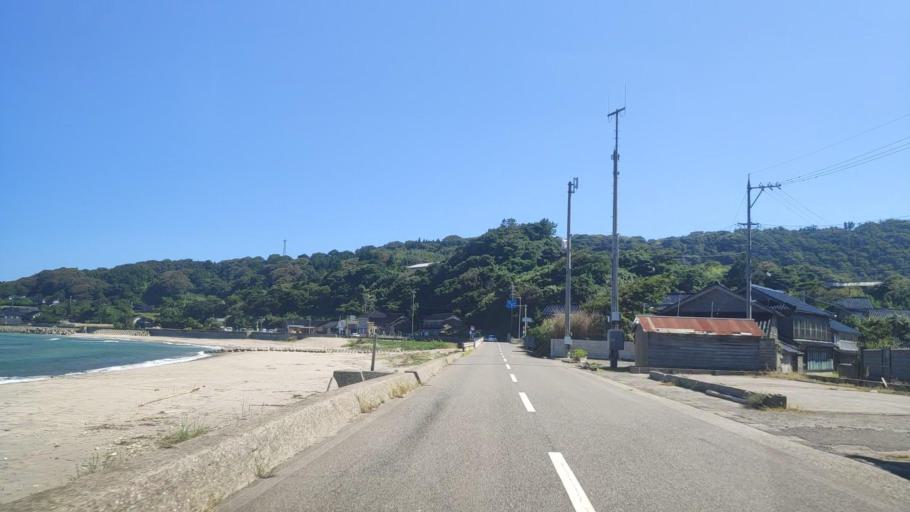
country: JP
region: Ishikawa
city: Nanao
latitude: 37.5272
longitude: 137.2808
